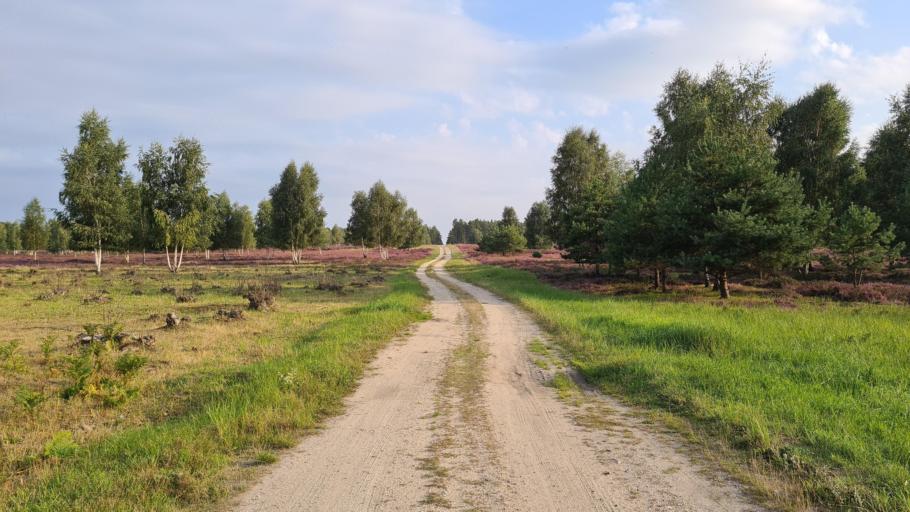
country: DE
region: Brandenburg
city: Schonborn
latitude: 51.6404
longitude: 13.4949
